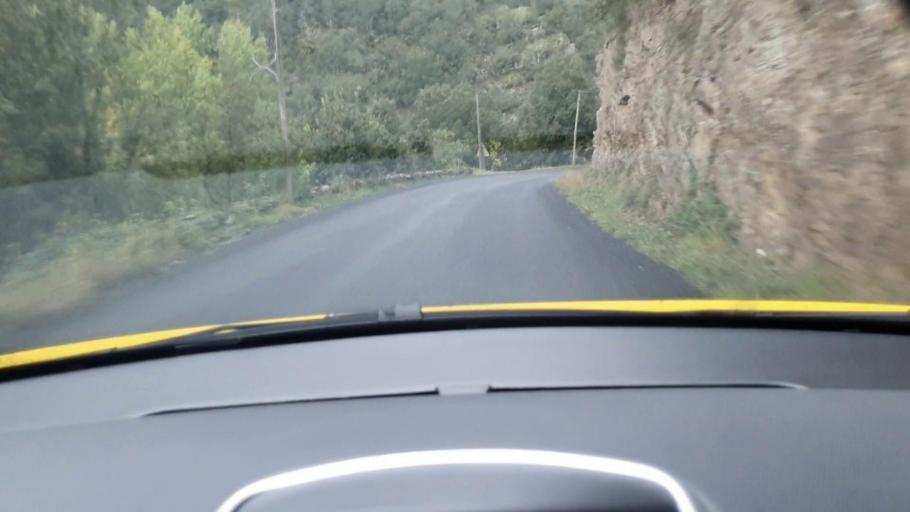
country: FR
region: Languedoc-Roussillon
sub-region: Departement du Gard
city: Sumene
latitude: 44.0195
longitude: 3.7301
